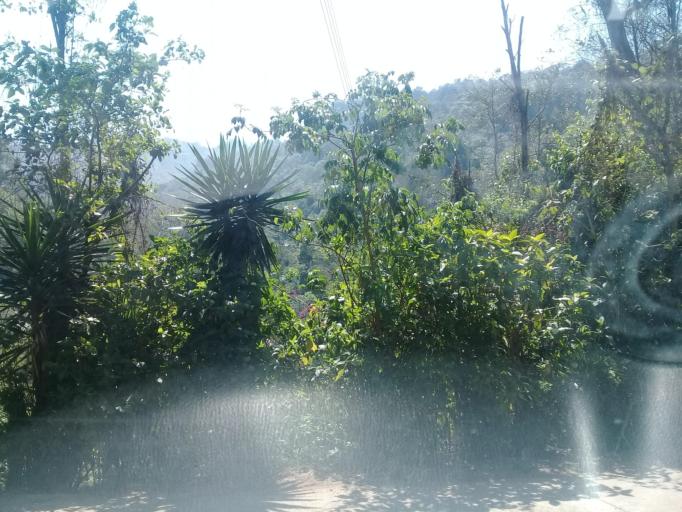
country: MX
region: Veracruz
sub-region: Tlilapan
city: Tonalixco
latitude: 18.7586
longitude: -97.0415
